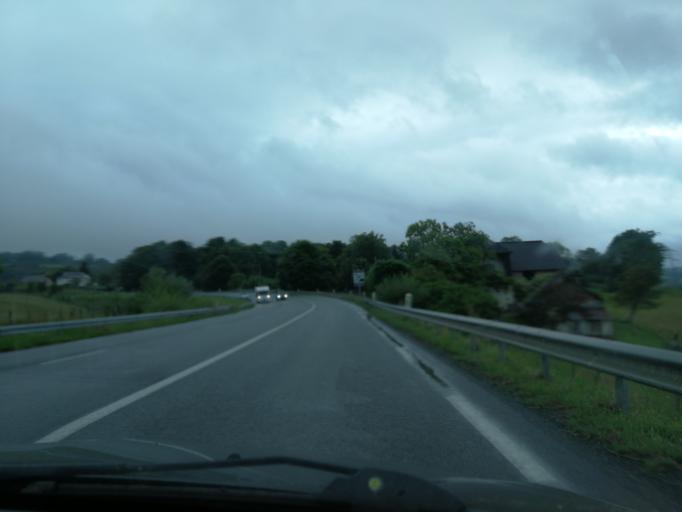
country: FR
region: Aquitaine
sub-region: Departement des Pyrenees-Atlantiques
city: Arudy
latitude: 43.1731
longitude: -0.4400
